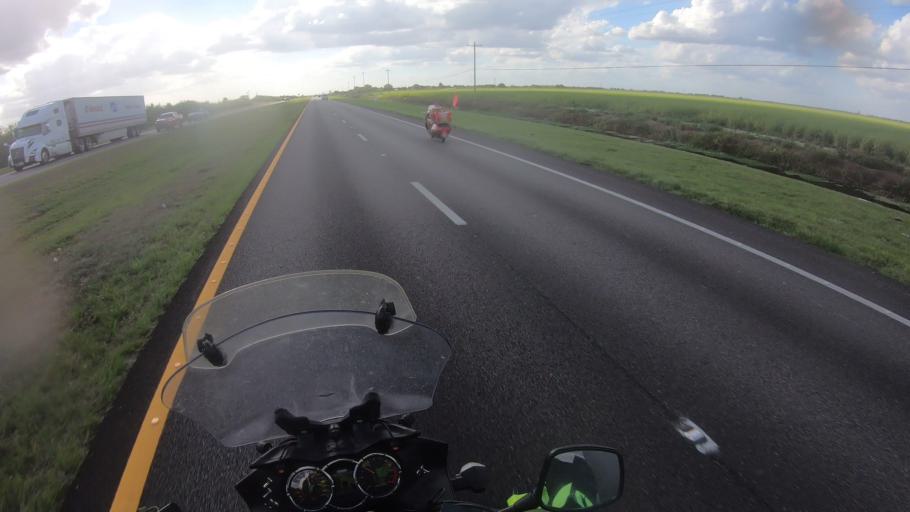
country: US
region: Florida
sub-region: Glades County
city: Moore Haven
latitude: 26.8328
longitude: -81.1337
